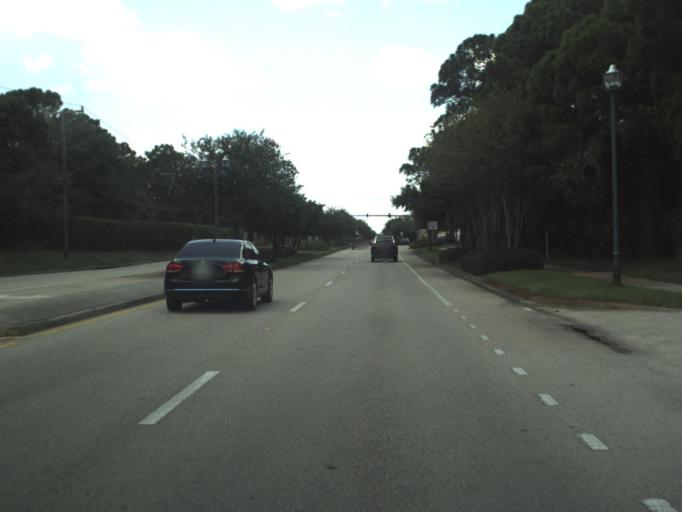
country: US
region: Florida
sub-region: Martin County
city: Palm City
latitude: 27.1638
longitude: -80.2328
